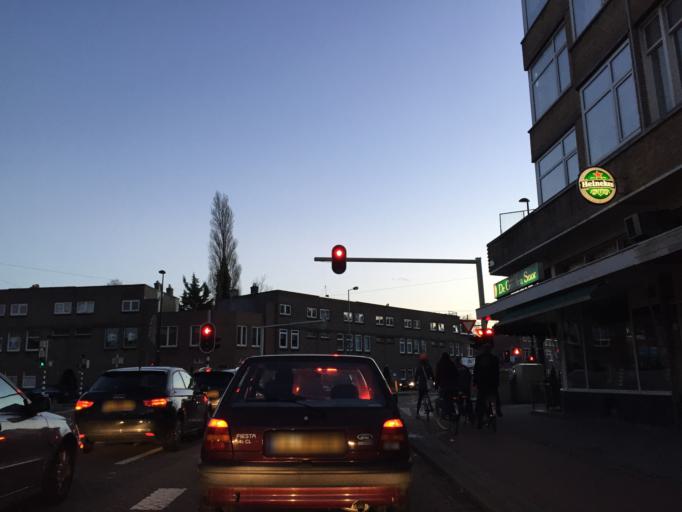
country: NL
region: South Holland
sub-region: Gemeente Rotterdam
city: Rotterdam
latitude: 51.9457
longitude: 4.4743
